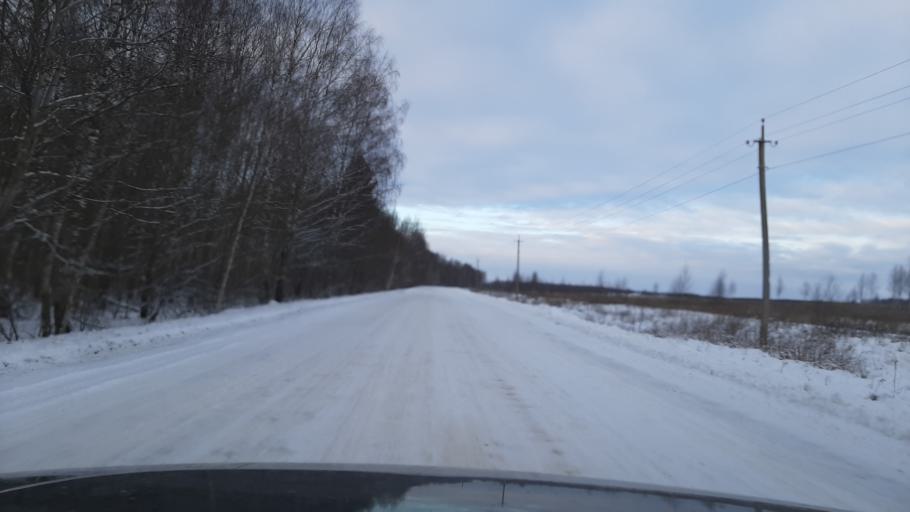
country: RU
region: Kostroma
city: Nerekhta
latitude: 57.4705
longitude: 40.6818
